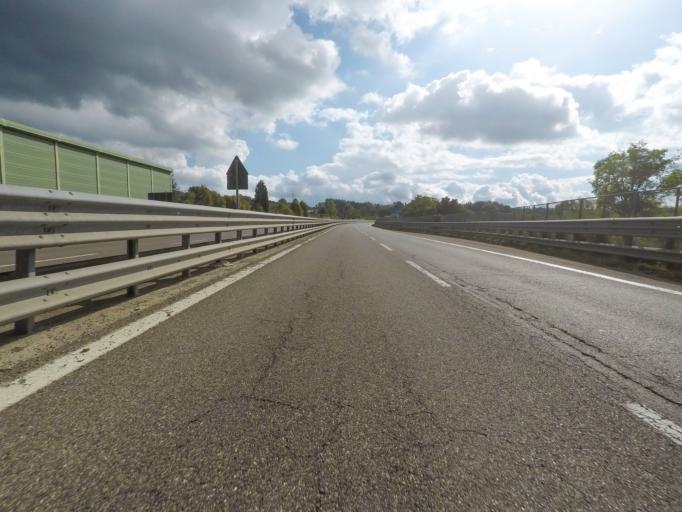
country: IT
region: Tuscany
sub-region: Provincia di Siena
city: Rapolano Terme
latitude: 43.3037
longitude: 11.5945
